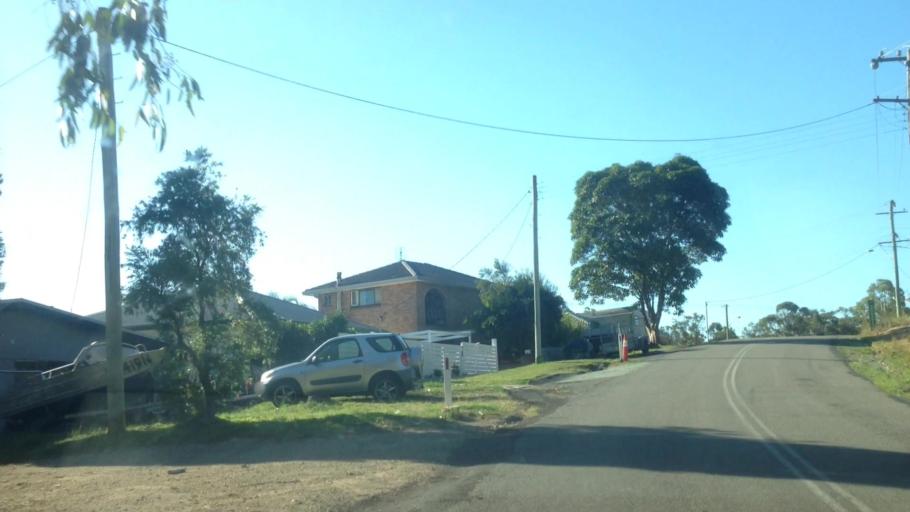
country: AU
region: New South Wales
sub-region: Lake Macquarie Shire
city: Arcadia vale
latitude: -33.1087
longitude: 151.5588
